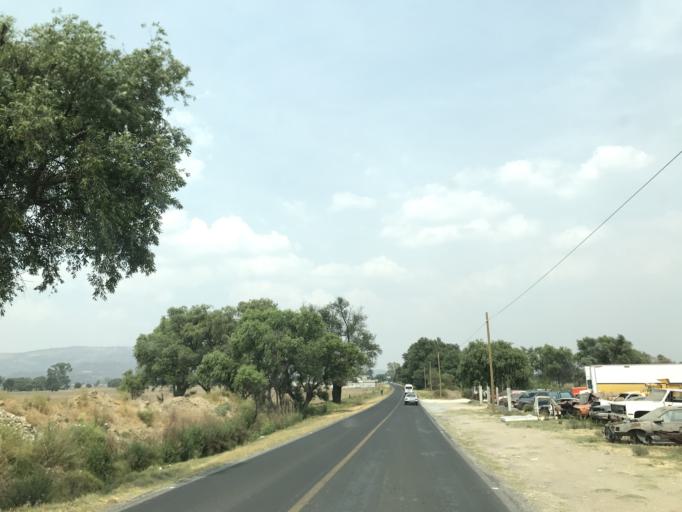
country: MX
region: Tlaxcala
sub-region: Ixtacuixtla de Mariano Matamoros
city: Santa Justina Ecatepec
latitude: 19.3140
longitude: -98.3333
